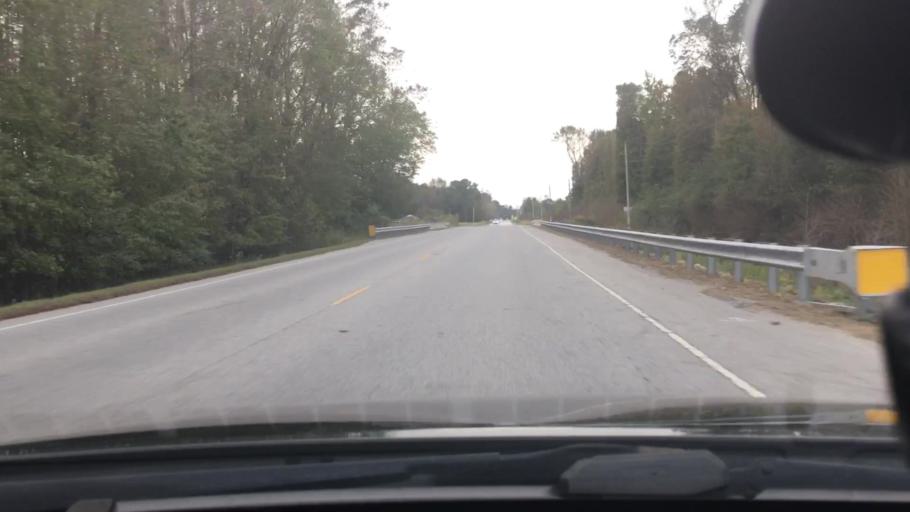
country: US
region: North Carolina
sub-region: Pitt County
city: Windsor
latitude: 35.4567
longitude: -77.2678
